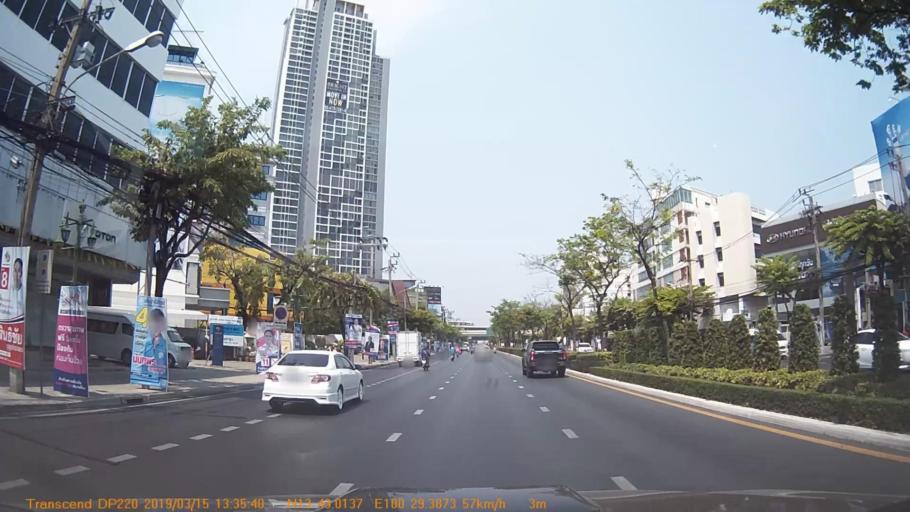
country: TH
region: Bangkok
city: Thon Buri
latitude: 13.7172
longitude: 100.4899
